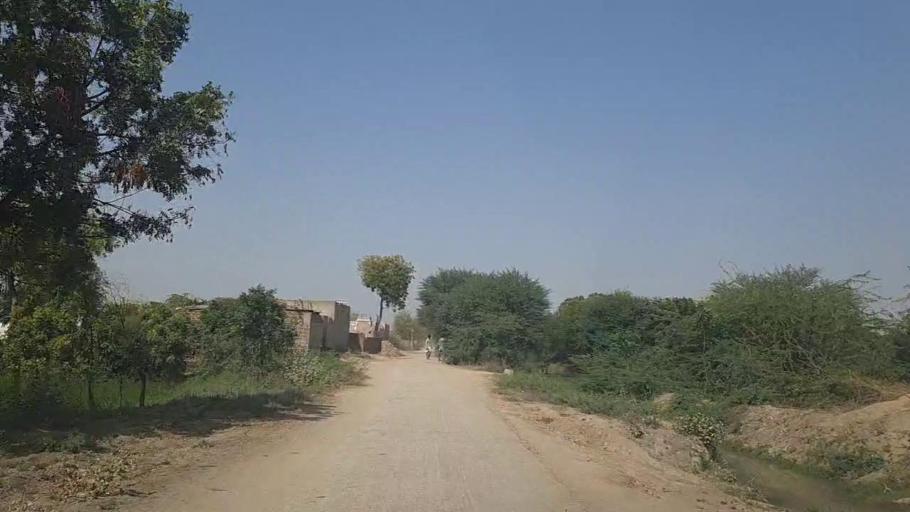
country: PK
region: Sindh
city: Naukot
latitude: 24.8467
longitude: 69.4395
